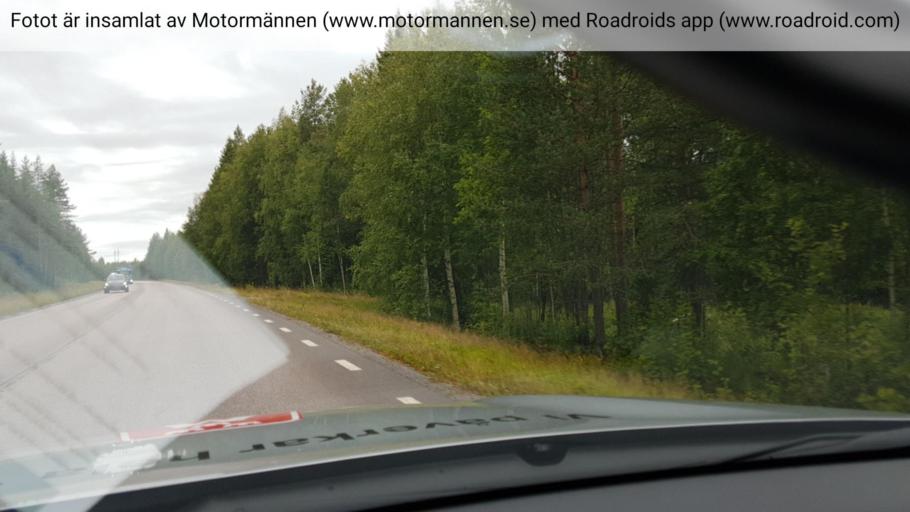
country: SE
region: Norrbotten
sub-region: Bodens Kommun
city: Boden
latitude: 65.8229
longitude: 21.6053
